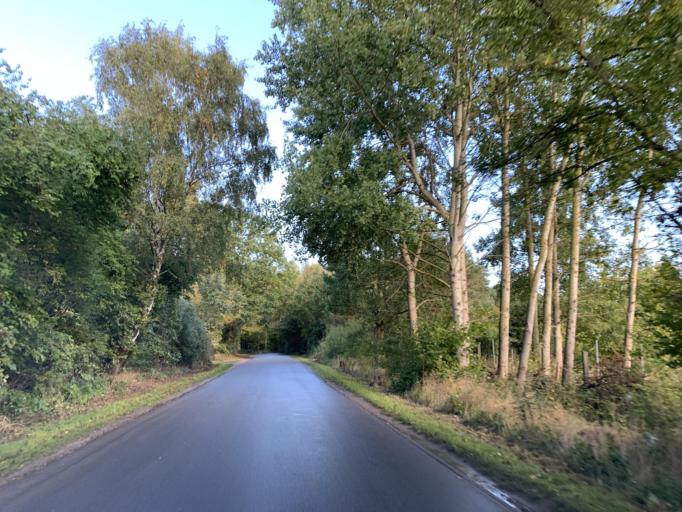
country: DE
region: Mecklenburg-Vorpommern
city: Blankensee
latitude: 53.4297
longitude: 13.2638
